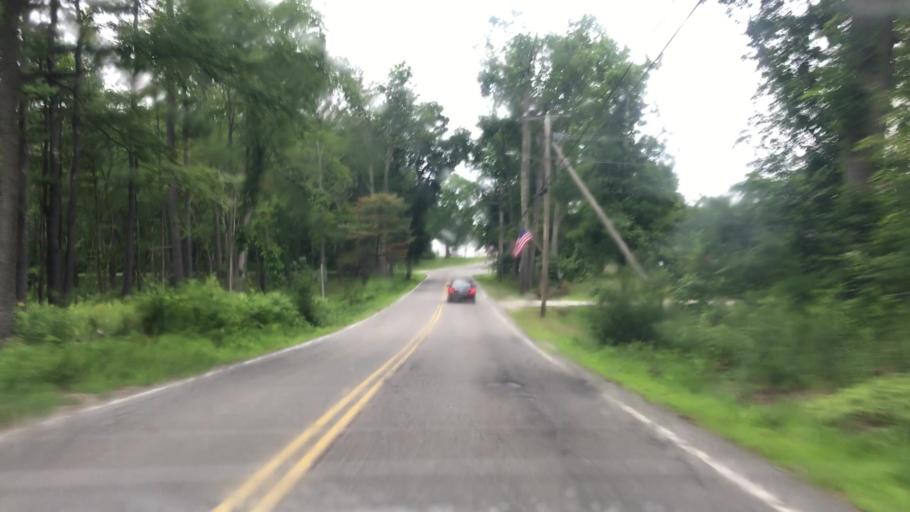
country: US
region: Maine
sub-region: York County
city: South Eliot
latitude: 43.1047
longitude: -70.8315
